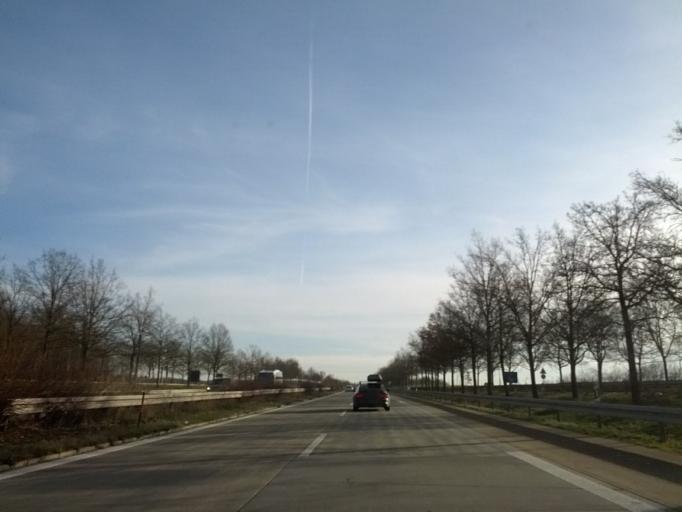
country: DE
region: Bavaria
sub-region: Regierungsbezirk Mittelfranken
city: Ohrenbach
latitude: 49.4847
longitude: 10.2127
